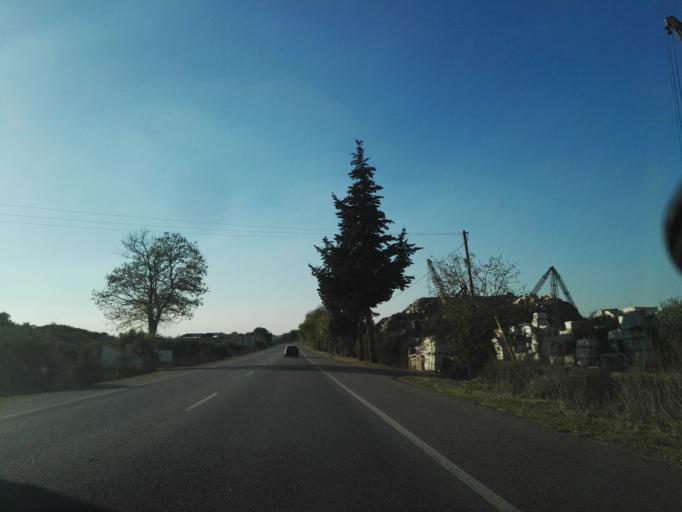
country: PT
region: Evora
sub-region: Estremoz
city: Estremoz
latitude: 38.8354
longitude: -7.5666
